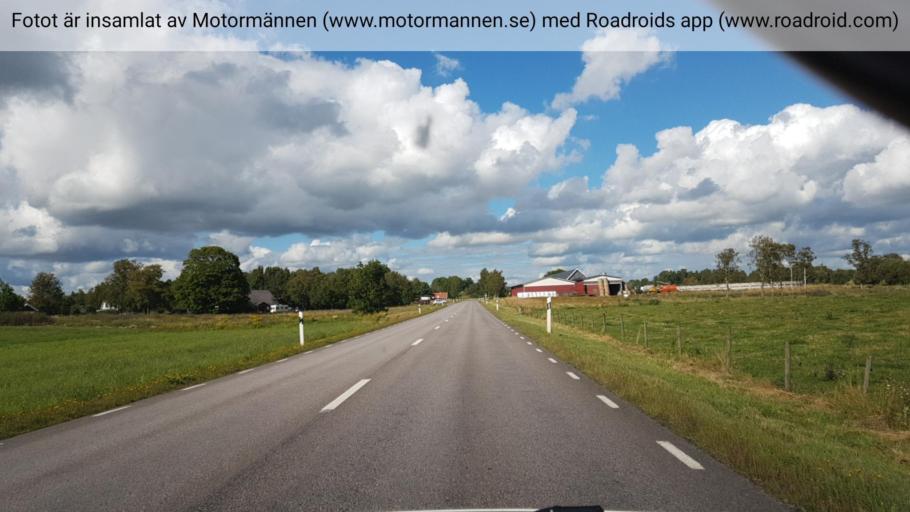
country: SE
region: Vaestra Goetaland
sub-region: Falkopings Kommun
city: Falkoeping
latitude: 58.0938
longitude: 13.5257
